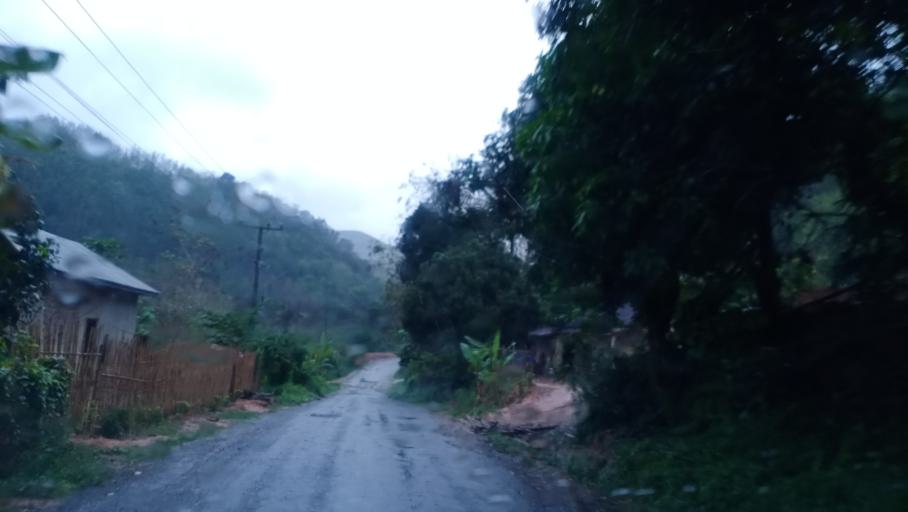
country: LA
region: Phongsali
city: Khoa
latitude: 21.0637
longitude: 102.4755
